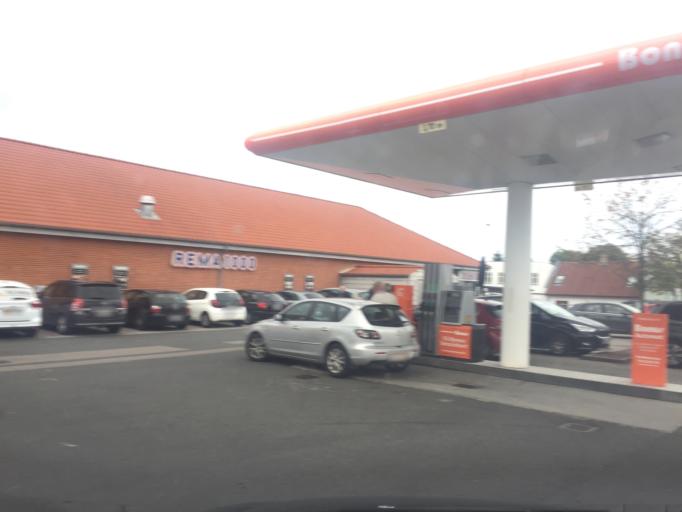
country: DK
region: Zealand
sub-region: Slagelse Kommune
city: Slagelse
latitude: 55.4115
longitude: 11.3368
